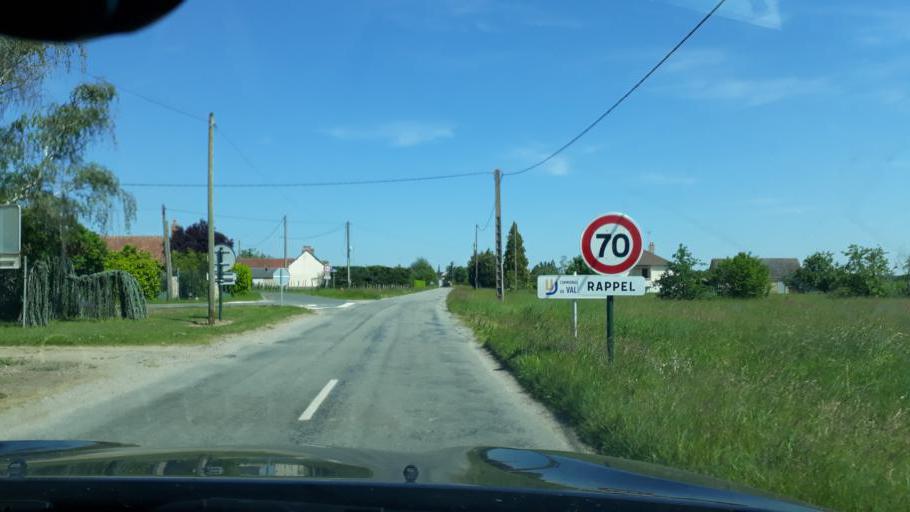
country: FR
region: Centre
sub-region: Departement du Loiret
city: Saint-Benoit-sur-Loire
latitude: 47.8053
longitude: 2.2681
